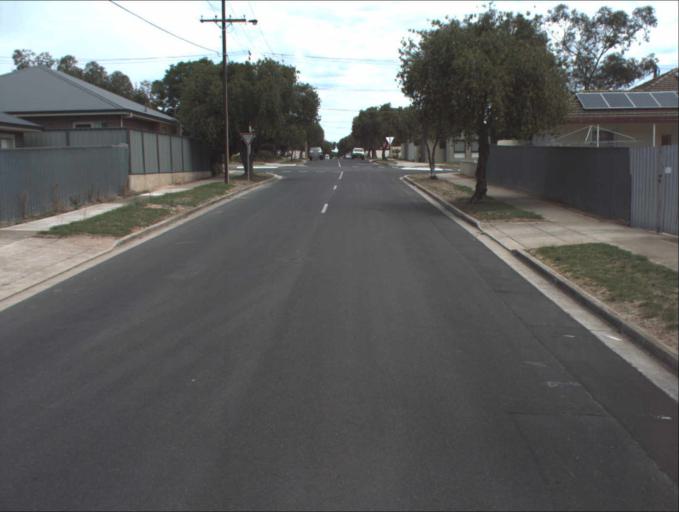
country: AU
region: South Australia
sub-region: Port Adelaide Enfield
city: Enfield
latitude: -34.8497
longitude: 138.6162
